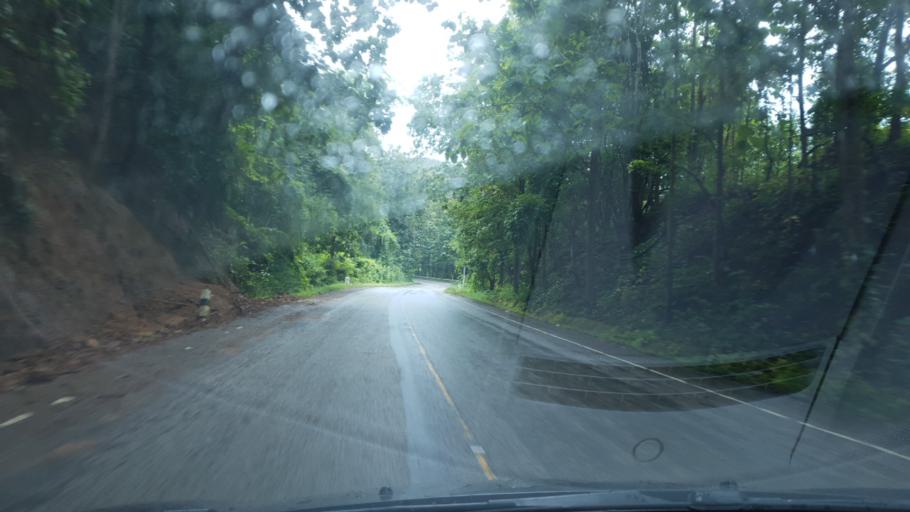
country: TH
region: Mae Hong Son
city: Pa Pae
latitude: 18.2773
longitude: 97.9394
